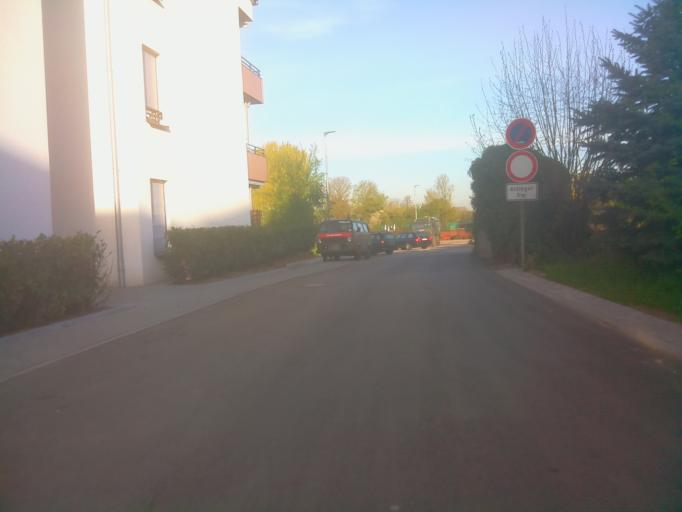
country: DE
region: Baden-Wuerttemberg
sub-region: Karlsruhe Region
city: Weinheim
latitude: 49.5136
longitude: 8.6558
